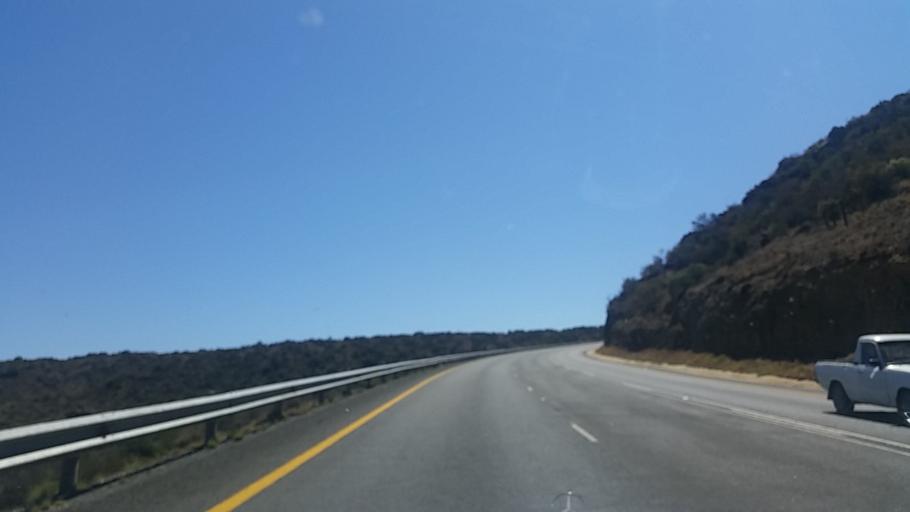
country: ZA
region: Eastern Cape
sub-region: Cacadu District Municipality
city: Graaff-Reinet
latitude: -32.0608
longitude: 24.6075
